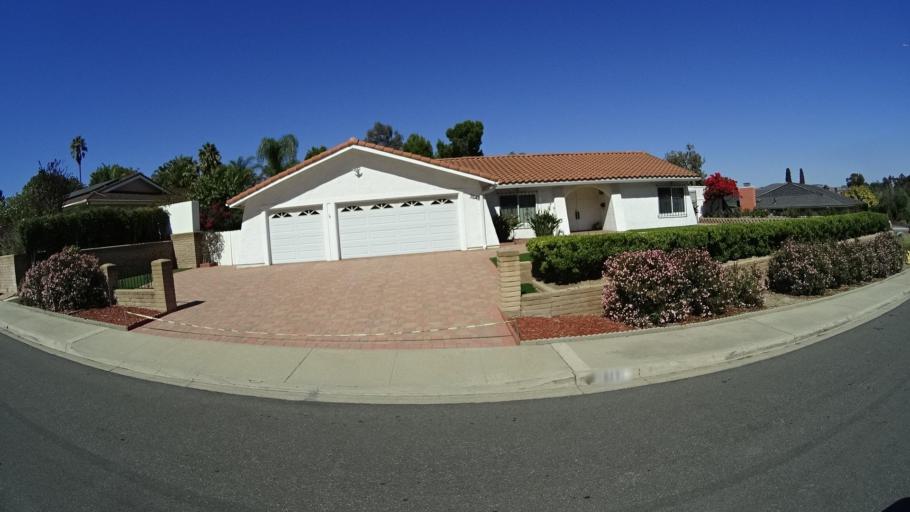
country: US
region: California
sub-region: San Diego County
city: Bonita
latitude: 32.6634
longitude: -117.0168
